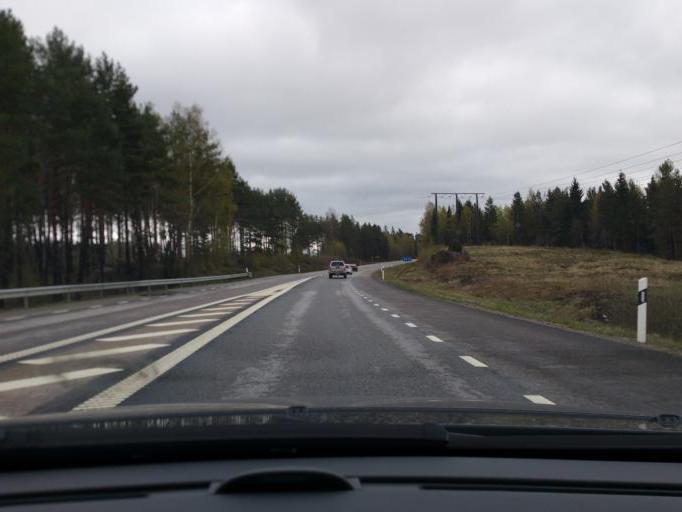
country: SE
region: Kronoberg
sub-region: Vaxjo Kommun
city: Vaexjoe
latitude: 56.8618
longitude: 14.8500
